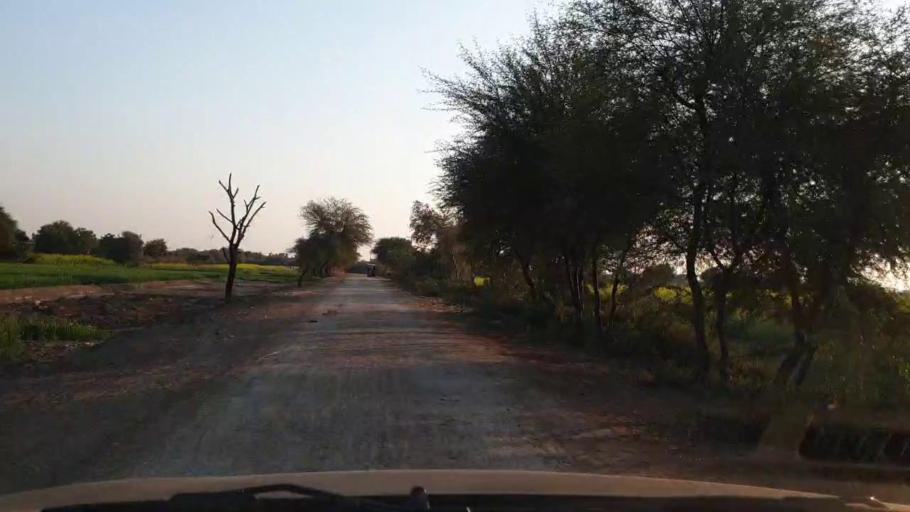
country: PK
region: Sindh
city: Jhol
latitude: 25.9209
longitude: 68.9336
